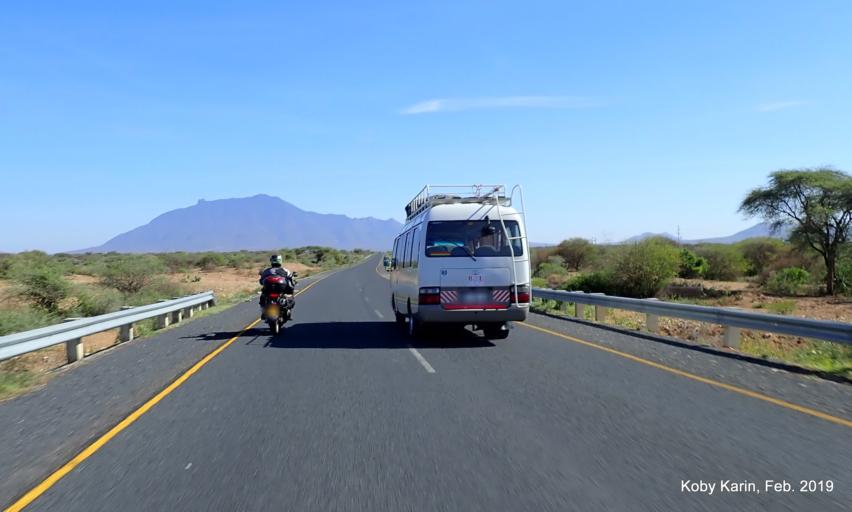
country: TZ
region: Arusha
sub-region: Longido District
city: Longido
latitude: -2.8669
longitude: 36.7031
